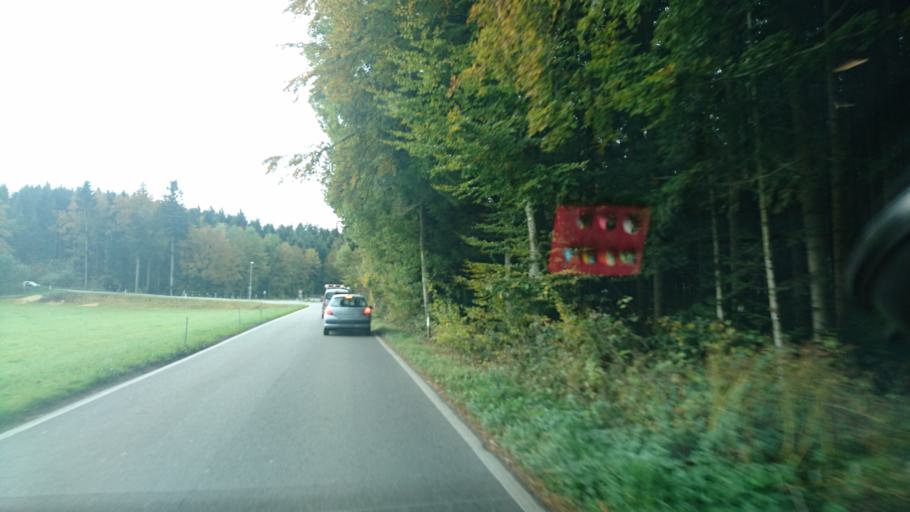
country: CH
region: Bern
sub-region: Bern-Mittelland District
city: Kirchlindach
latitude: 46.9872
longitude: 7.4121
